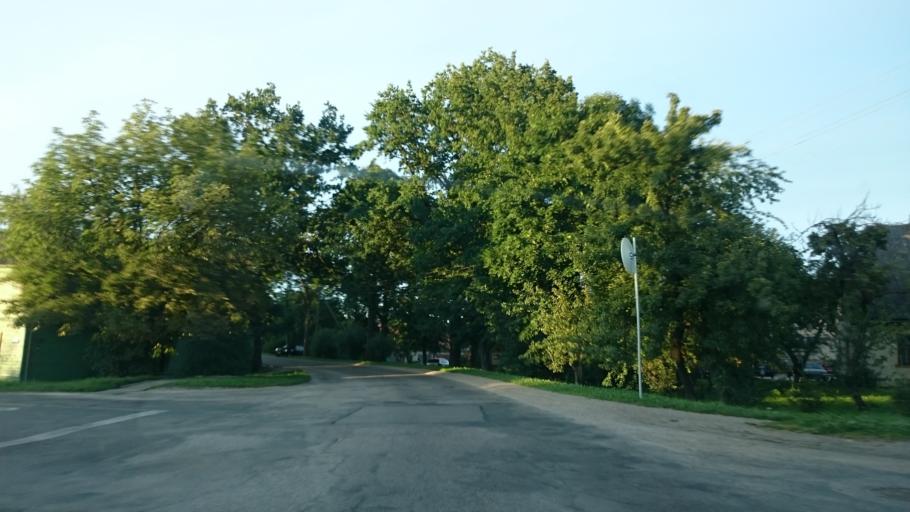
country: LV
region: Saldus Rajons
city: Saldus
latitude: 56.6696
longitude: 22.4933
